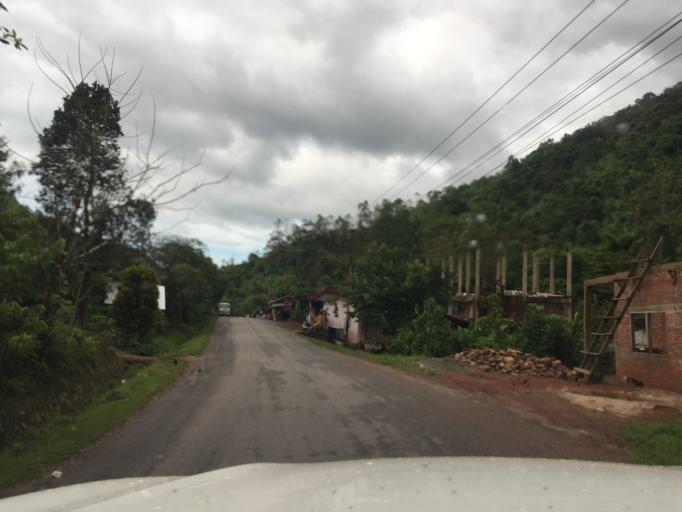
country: LA
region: Oudomxai
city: Muang La
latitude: 20.8150
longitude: 102.0919
